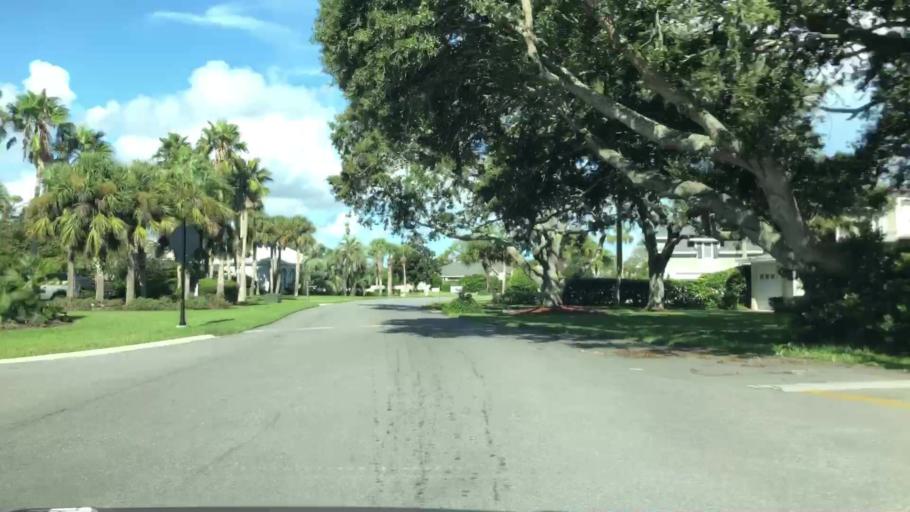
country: US
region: Florida
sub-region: Saint Johns County
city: Ponte Vedra Beach
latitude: 30.2429
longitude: -81.3831
